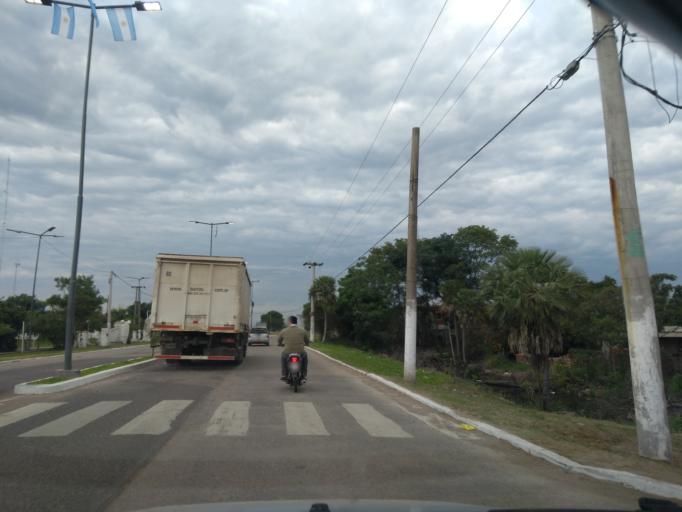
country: AR
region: Chaco
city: Puerto Vilelas
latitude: -27.5162
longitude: -58.9419
